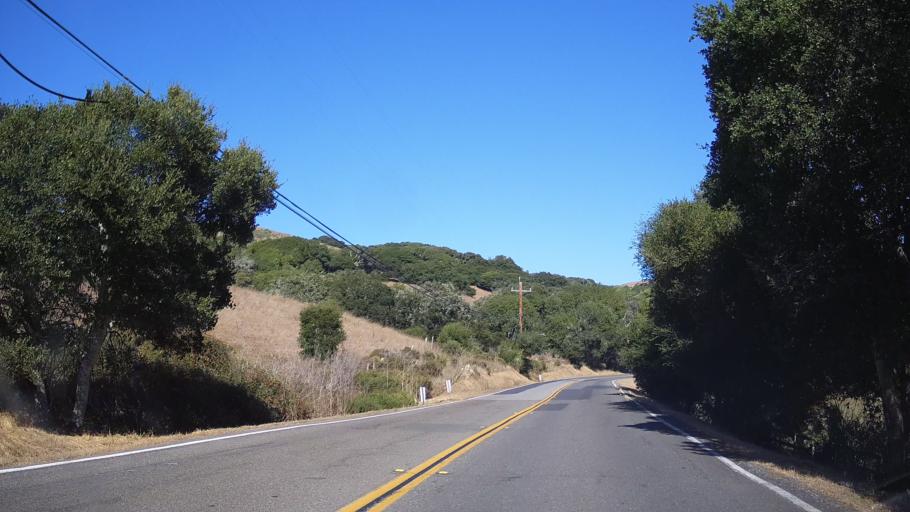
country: US
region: California
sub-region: Marin County
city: Inverness
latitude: 38.0753
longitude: -122.7976
